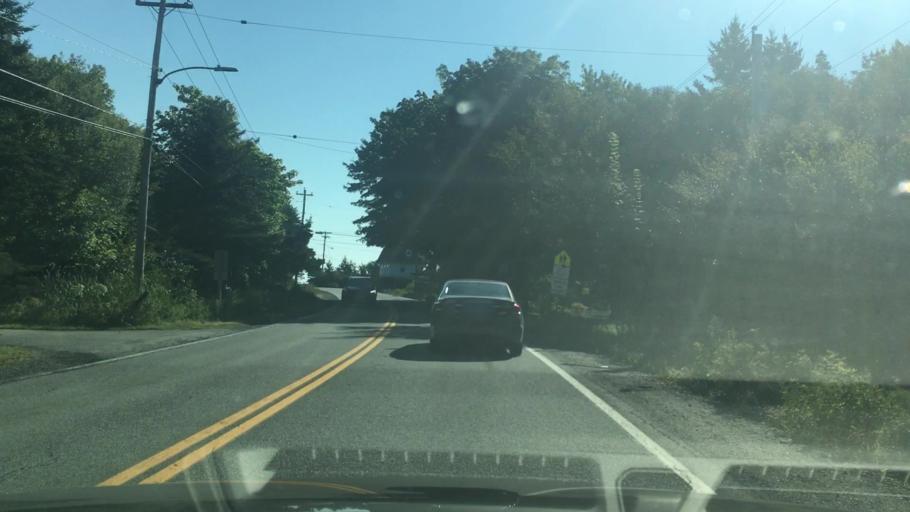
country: CA
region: Nova Scotia
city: Cole Harbour
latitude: 44.7832
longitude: -63.1565
